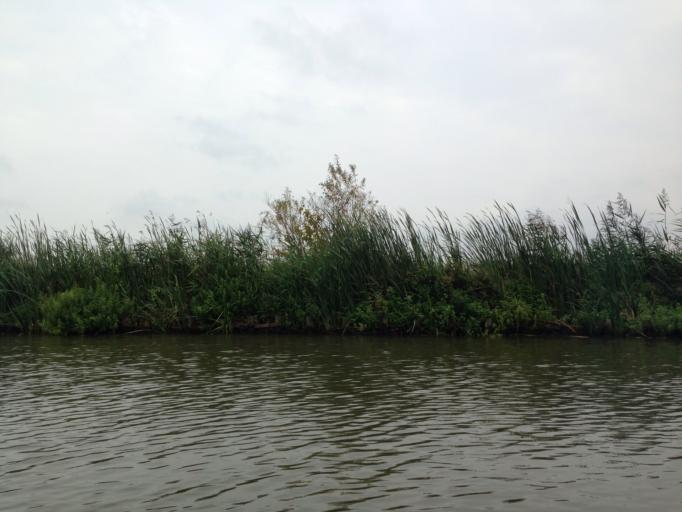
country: NL
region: South Holland
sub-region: Gemeente Vlaardingen
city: Vlaardingen
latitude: 51.9452
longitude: 4.3173
